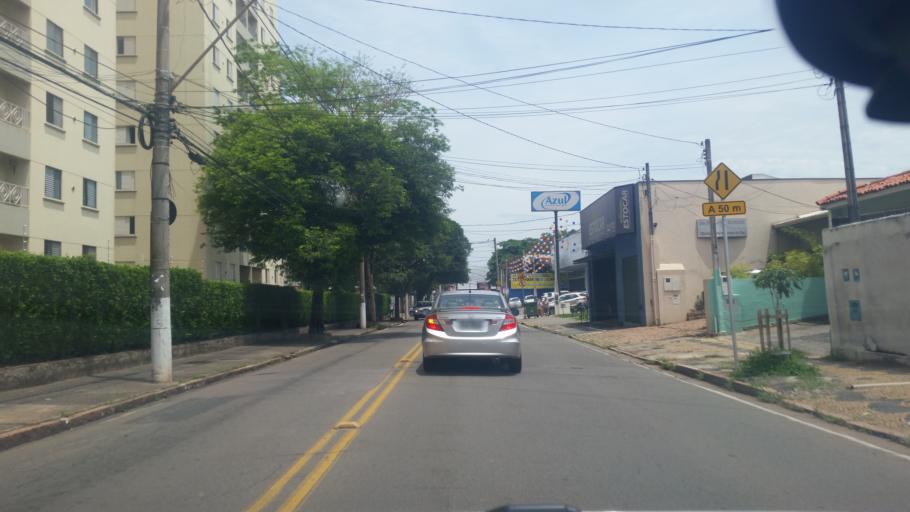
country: BR
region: Sao Paulo
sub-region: Campinas
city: Campinas
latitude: -22.8870
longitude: -47.0622
